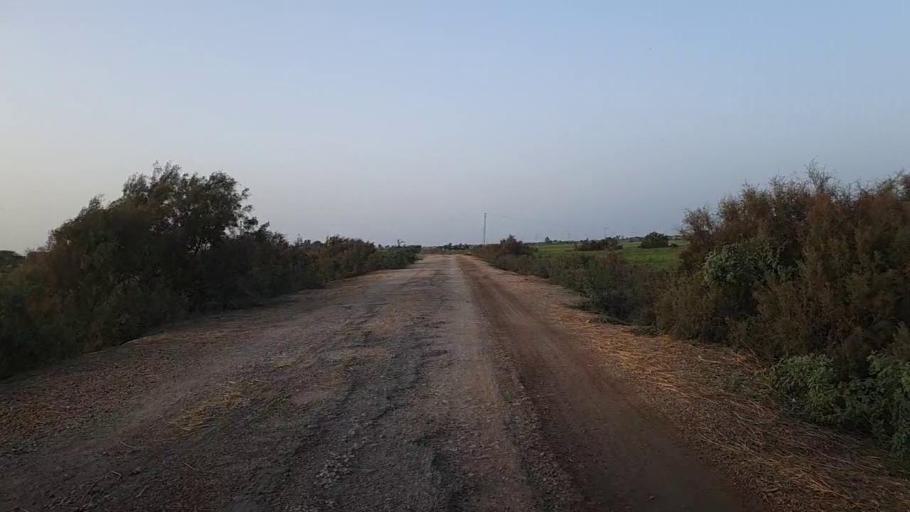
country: PK
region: Sindh
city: Kario
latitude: 24.7264
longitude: 68.4610
